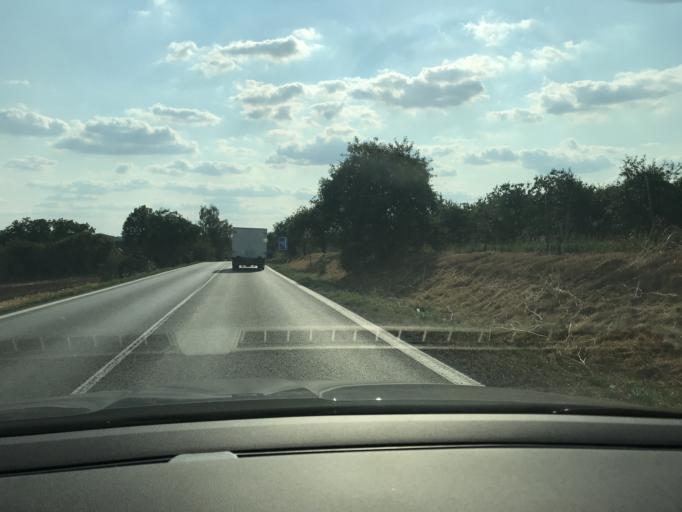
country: CZ
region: Central Bohemia
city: Brandysek
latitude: 50.2557
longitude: 14.1637
